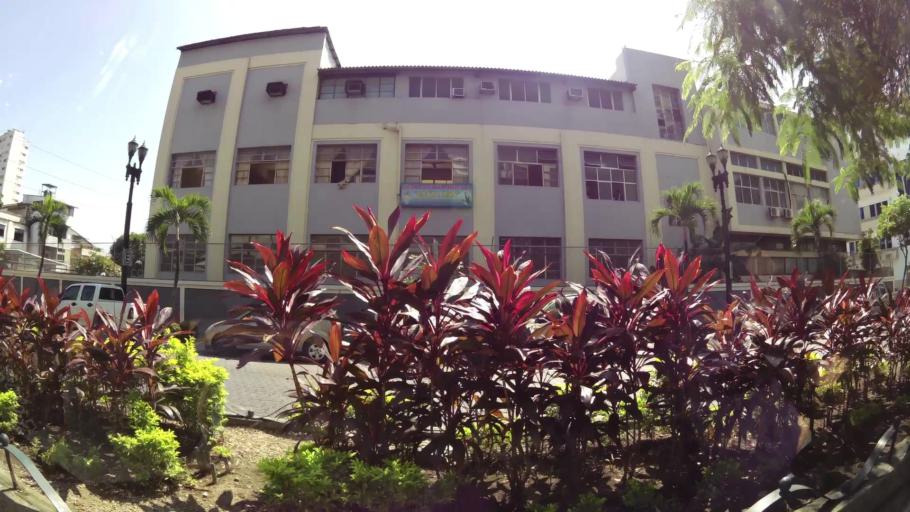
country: EC
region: Guayas
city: Guayaquil
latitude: -2.1883
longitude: -79.8923
